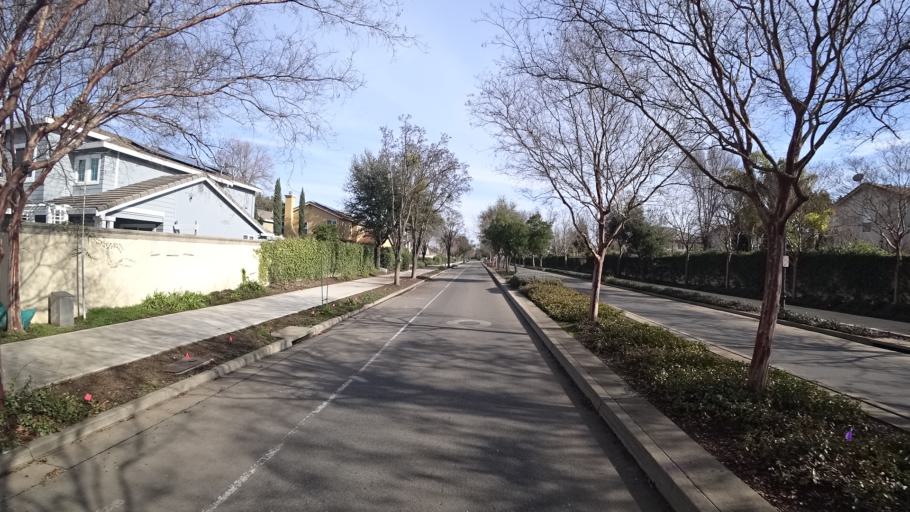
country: US
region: California
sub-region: Yolo County
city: Davis
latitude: 38.5580
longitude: -121.7019
